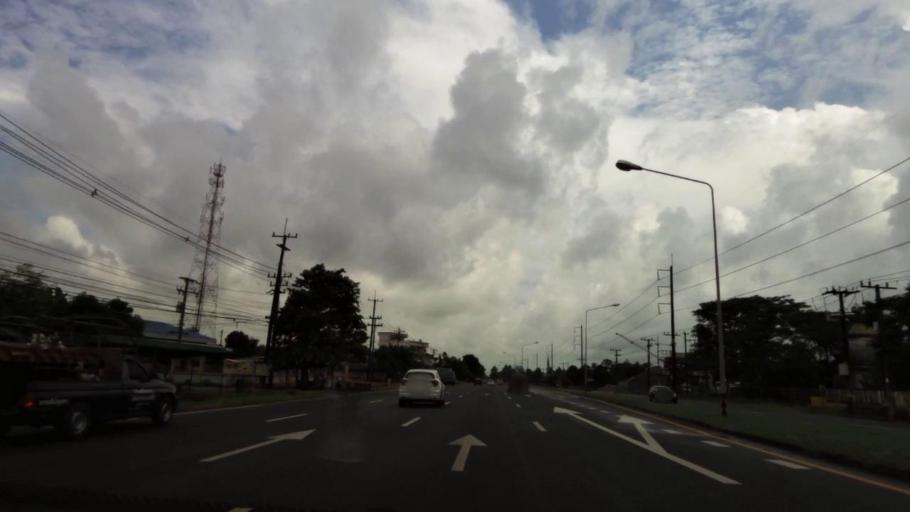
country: TH
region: Chanthaburi
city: Khlung
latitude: 12.5206
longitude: 102.1634
